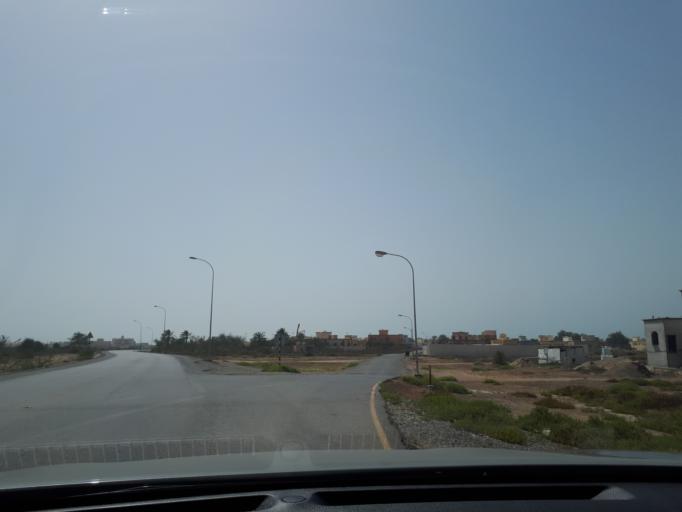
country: OM
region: Al Batinah
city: Barka'
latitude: 23.7020
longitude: 57.9409
